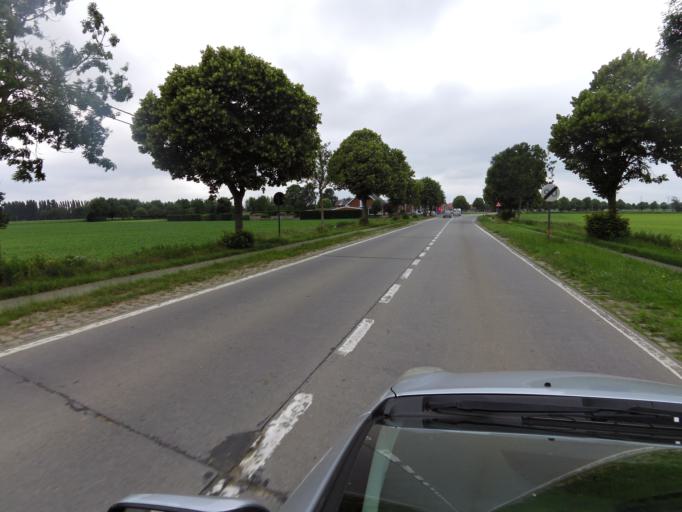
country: BE
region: Flanders
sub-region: Provincie West-Vlaanderen
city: Ieper
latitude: 50.9122
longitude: 2.8406
